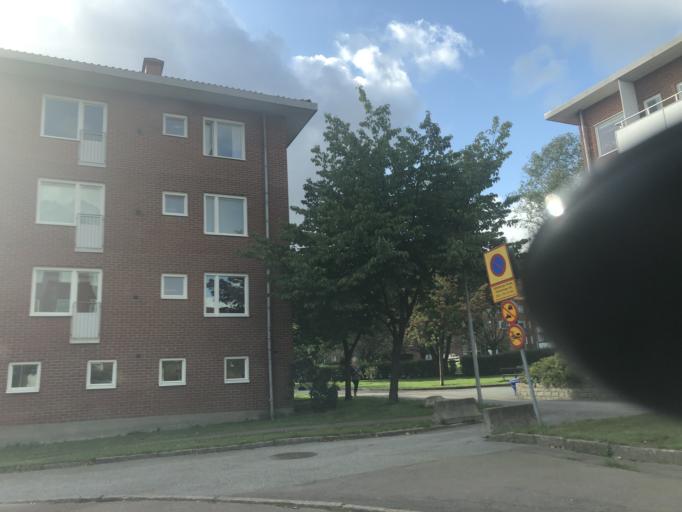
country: SE
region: Vaestra Goetaland
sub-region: Goteborg
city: Goeteborg
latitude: 57.7281
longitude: 11.9662
